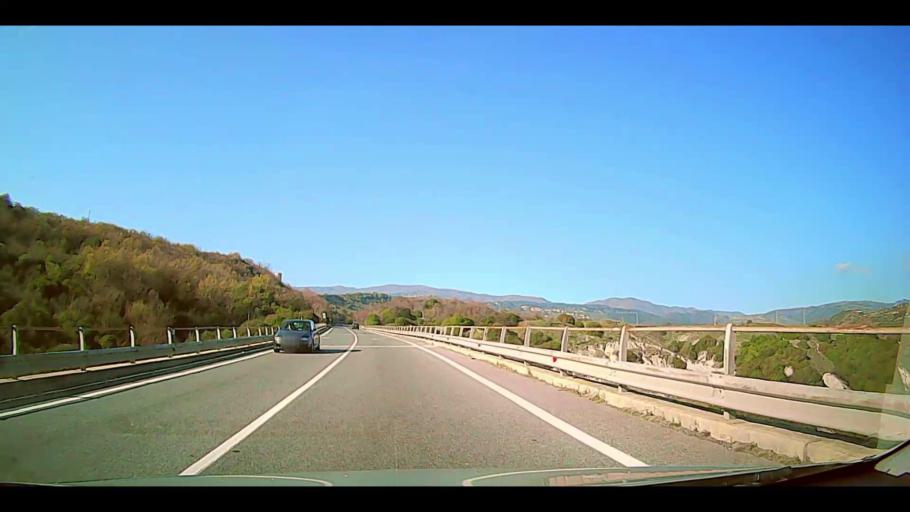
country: IT
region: Calabria
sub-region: Provincia di Crotone
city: Cotronei
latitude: 39.1872
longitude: 16.8264
